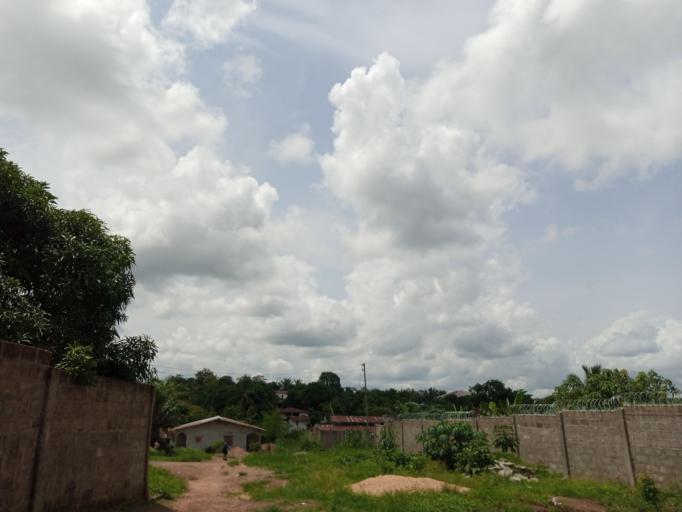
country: SL
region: Southern Province
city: Bo
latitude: 7.9421
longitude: -11.7194
